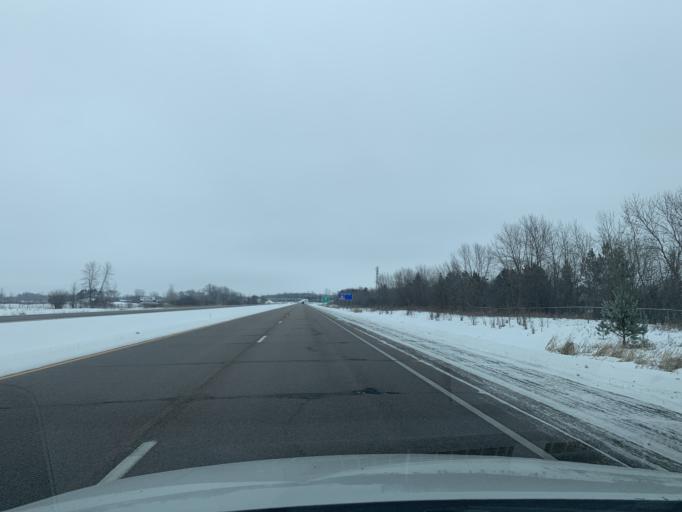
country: US
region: Minnesota
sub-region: Chisago County
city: Rush City
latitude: 45.6759
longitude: -92.9915
